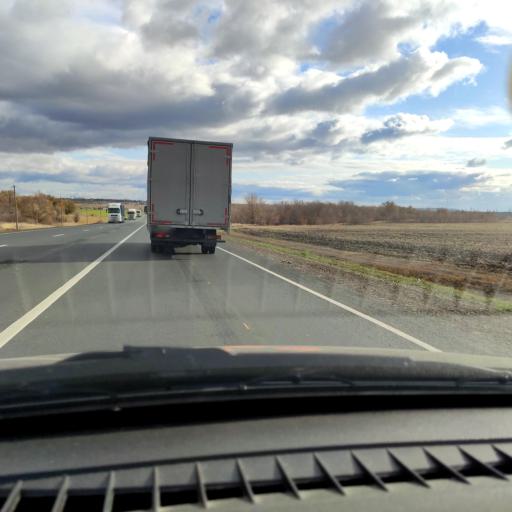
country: RU
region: Samara
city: Varlamovo
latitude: 53.2108
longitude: 48.4670
